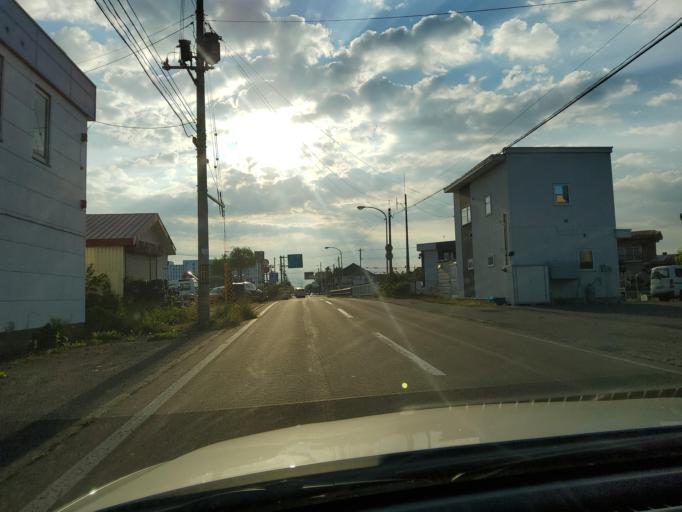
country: JP
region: Hokkaido
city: Obihiro
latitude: 42.9210
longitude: 143.1889
